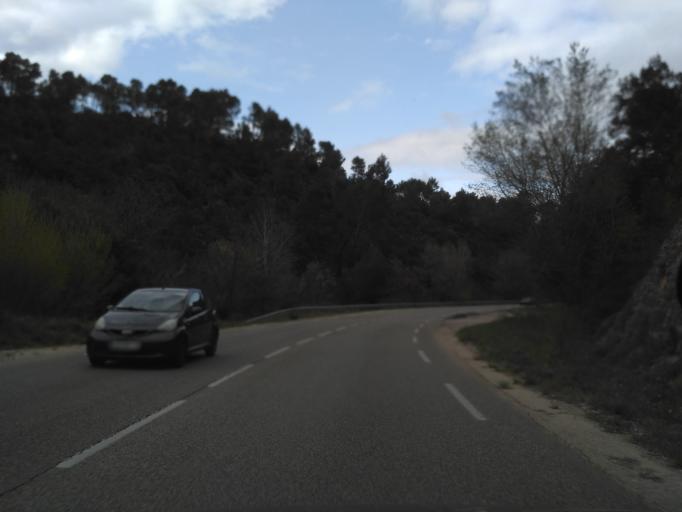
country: FR
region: Provence-Alpes-Cote d'Azur
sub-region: Departement du Var
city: Barjols
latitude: 43.5712
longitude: 6.0129
